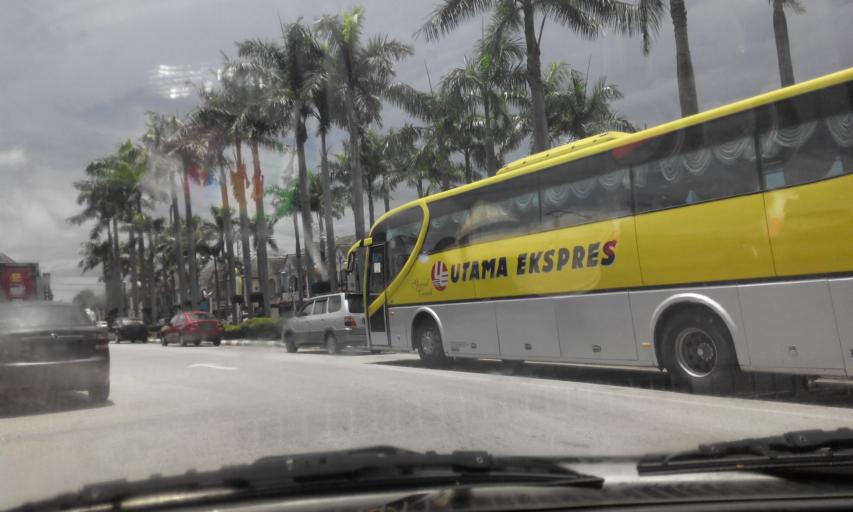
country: MY
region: Perak
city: Parit Buntar
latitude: 5.1187
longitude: 100.4875
